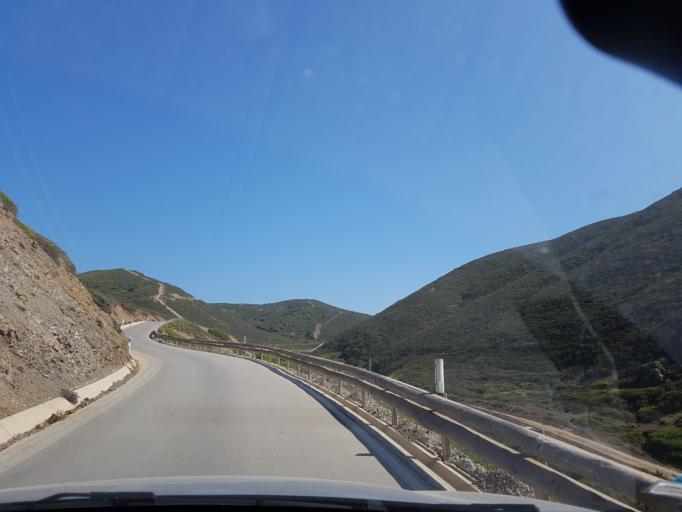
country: PT
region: Faro
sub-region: Vila do Bispo
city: Vila do Bispo
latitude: 37.1079
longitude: -8.9349
